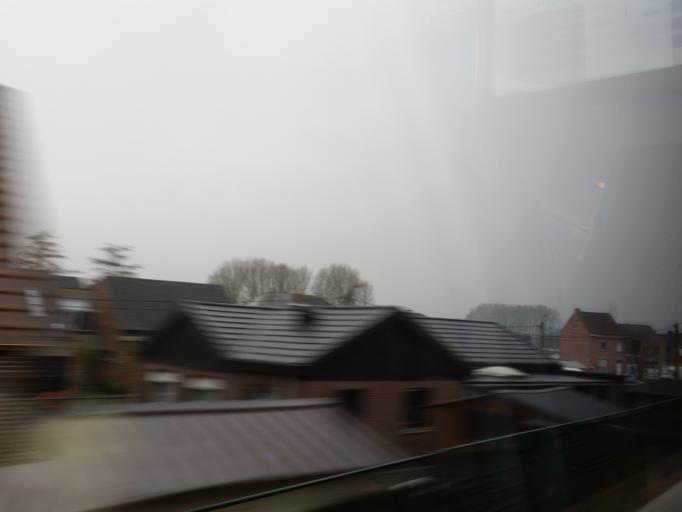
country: BE
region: Flanders
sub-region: Provincie Oost-Vlaanderen
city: Buggenhout
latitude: 51.0147
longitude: 4.2243
